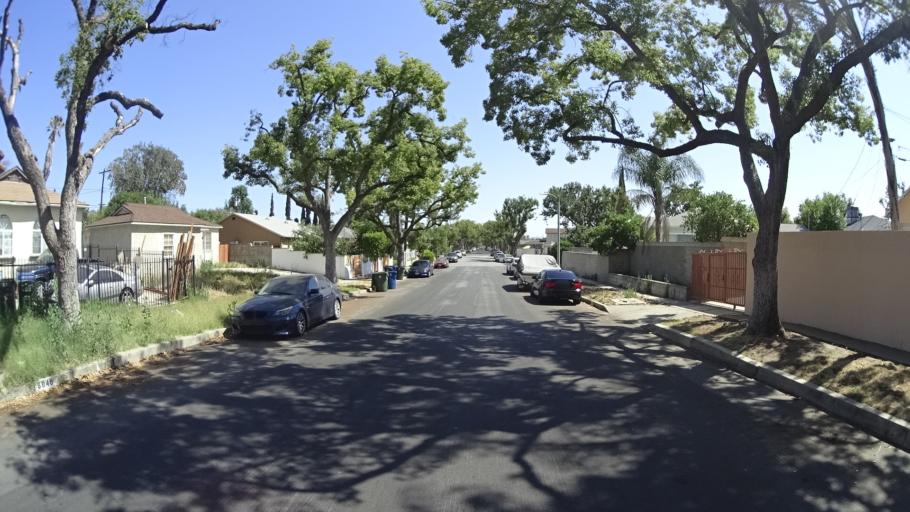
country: US
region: California
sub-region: Los Angeles County
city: Van Nuys
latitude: 34.2176
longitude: -118.4391
